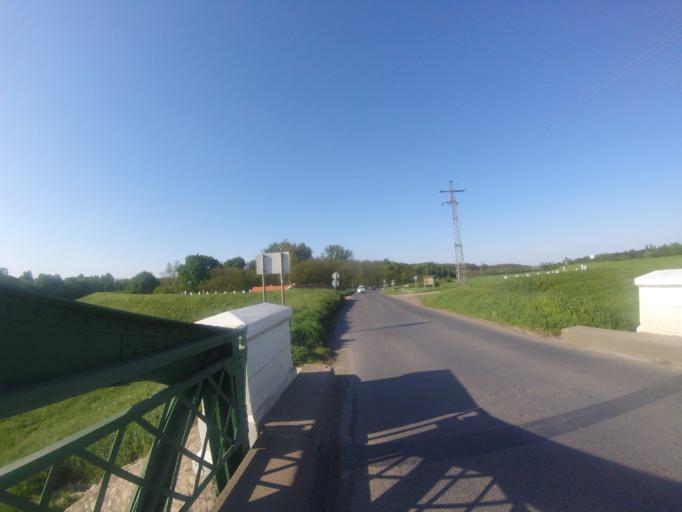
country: HU
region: Bekes
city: Gyula
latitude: 46.7008
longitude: 21.3128
